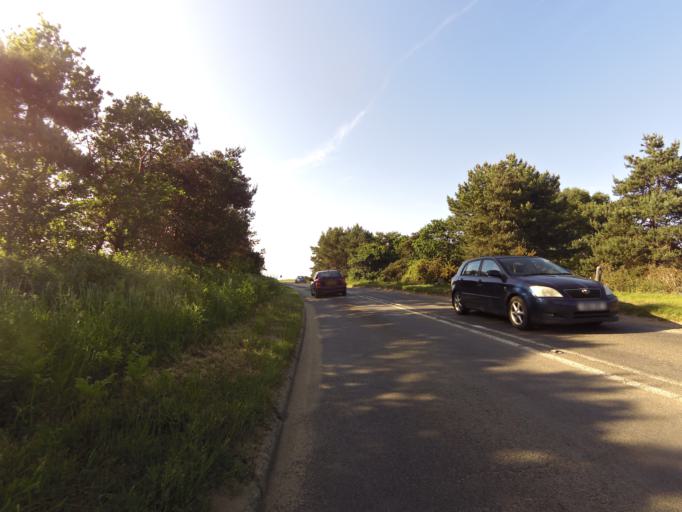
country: GB
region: England
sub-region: Suffolk
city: Woodbridge
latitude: 52.0779
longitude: 1.3636
